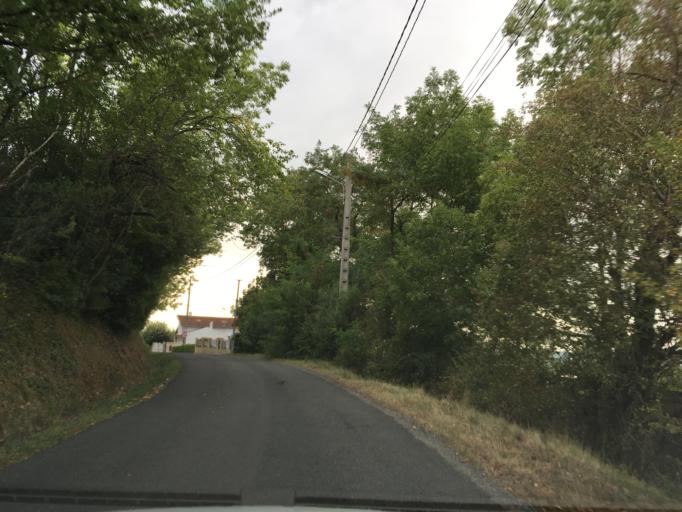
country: FR
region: Midi-Pyrenees
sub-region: Departement du Tarn
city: Castres
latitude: 43.6071
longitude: 2.2661
